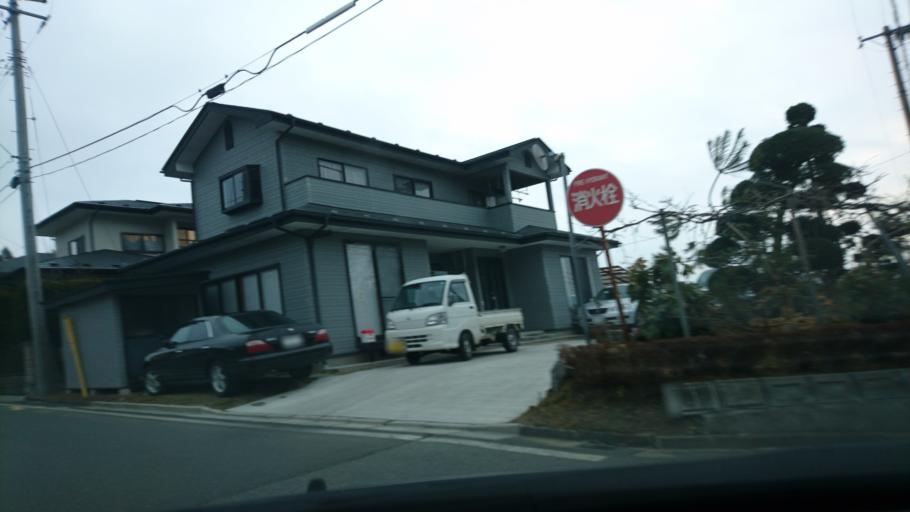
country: JP
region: Iwate
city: Ichinoseki
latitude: 38.9246
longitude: 141.3362
